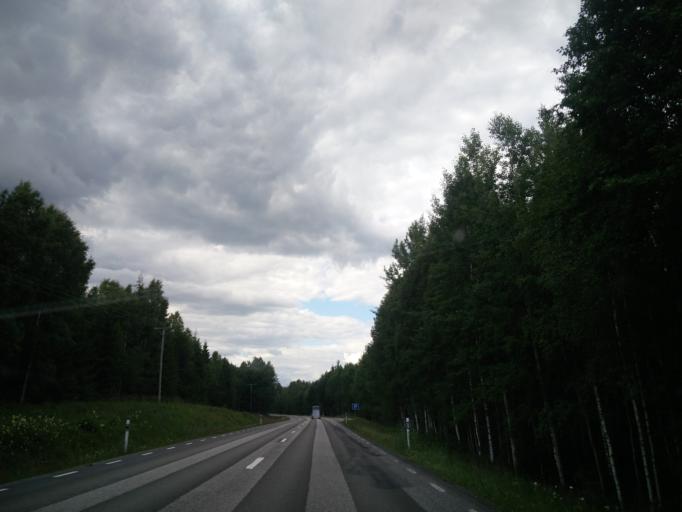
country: SE
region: OErebro
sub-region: Hallefors Kommun
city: Haellefors
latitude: 59.7798
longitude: 14.3850
